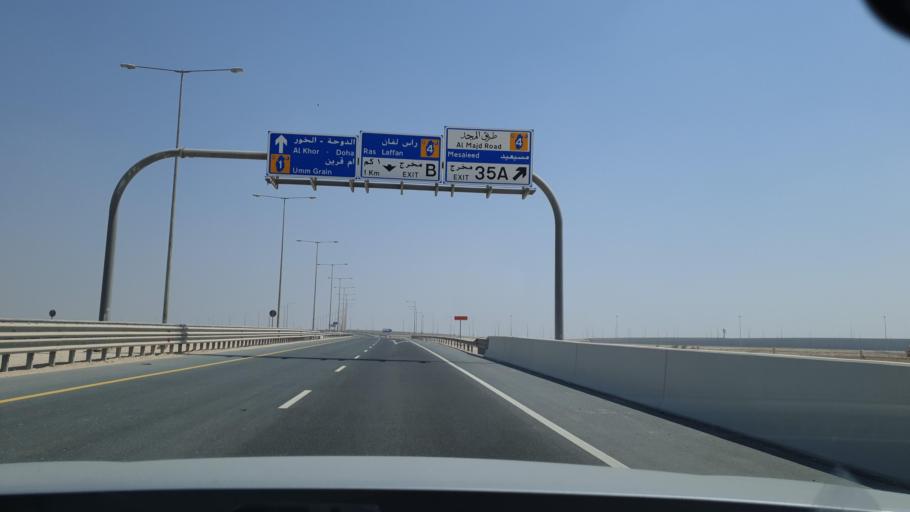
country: QA
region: Baladiyat az Za`ayin
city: Az Za`ayin
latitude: 25.6177
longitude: 51.3587
